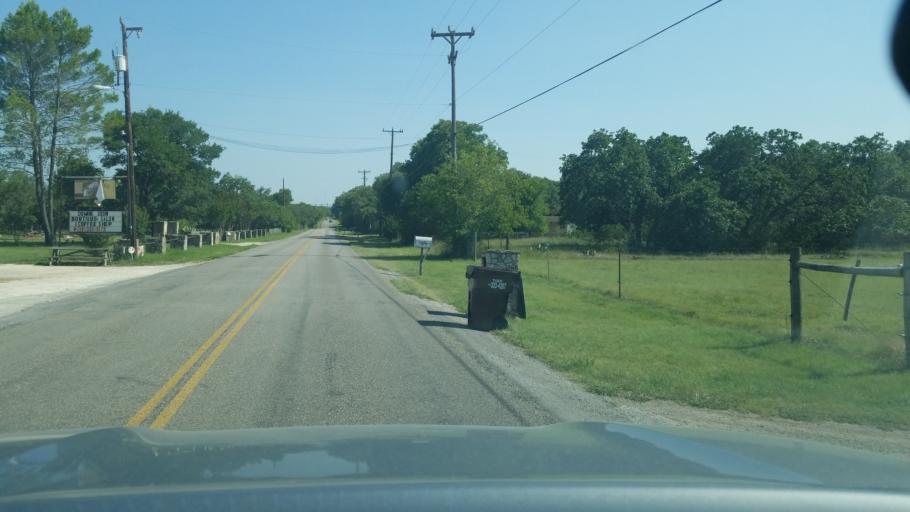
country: US
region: Texas
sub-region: Bexar County
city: Timberwood Park
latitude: 29.7512
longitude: -98.5128
